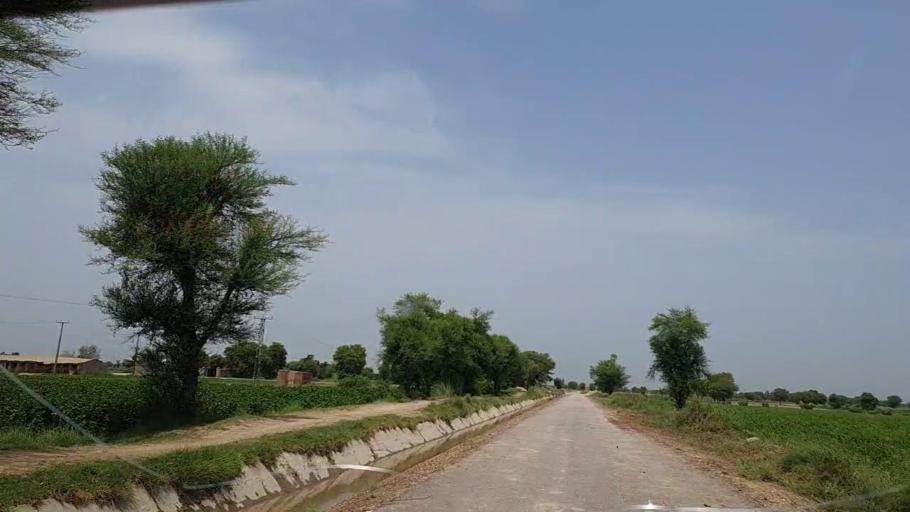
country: PK
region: Sindh
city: Tharu Shah
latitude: 26.9357
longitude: 68.0682
